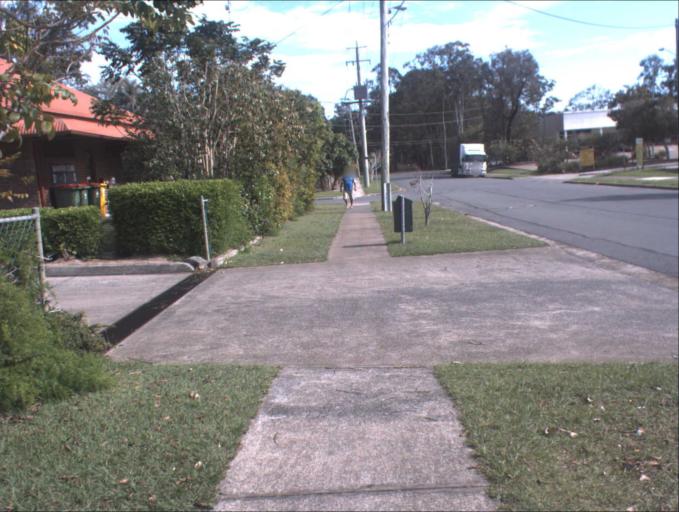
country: AU
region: Queensland
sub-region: Logan
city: Waterford West
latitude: -27.6809
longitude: 153.1141
